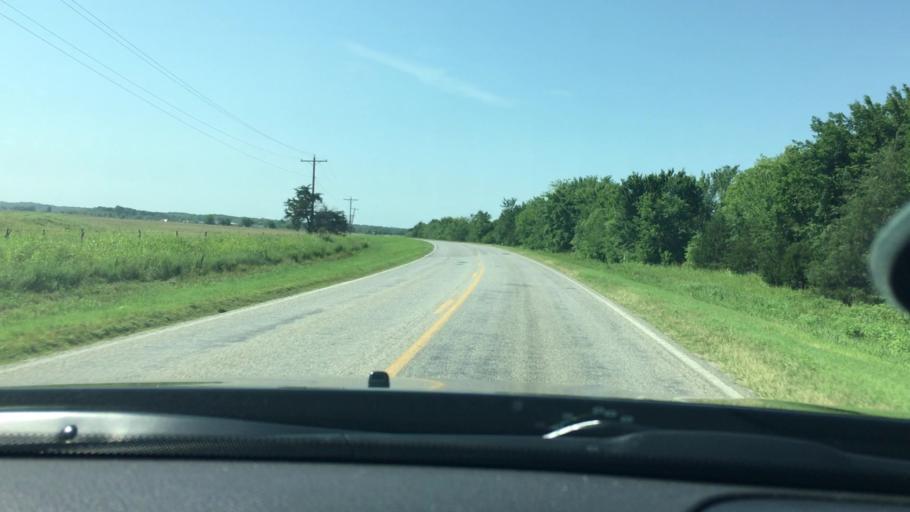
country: US
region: Oklahoma
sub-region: Coal County
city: Coalgate
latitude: 34.3515
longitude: -96.4246
